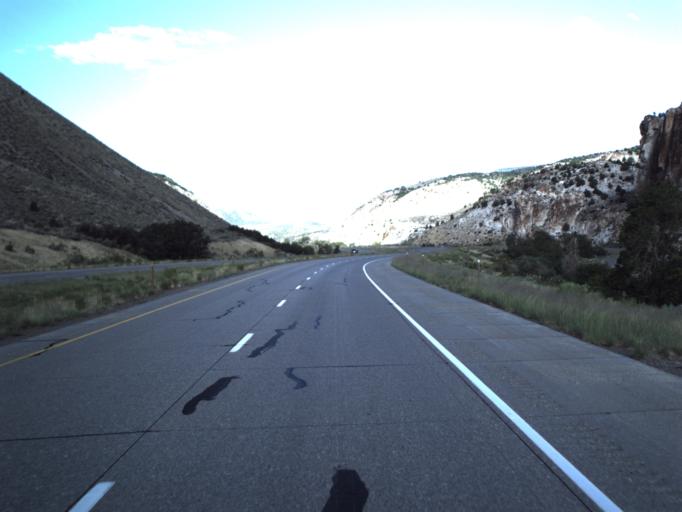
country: US
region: Utah
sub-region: Sevier County
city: Monroe
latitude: 38.5793
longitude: -112.2885
